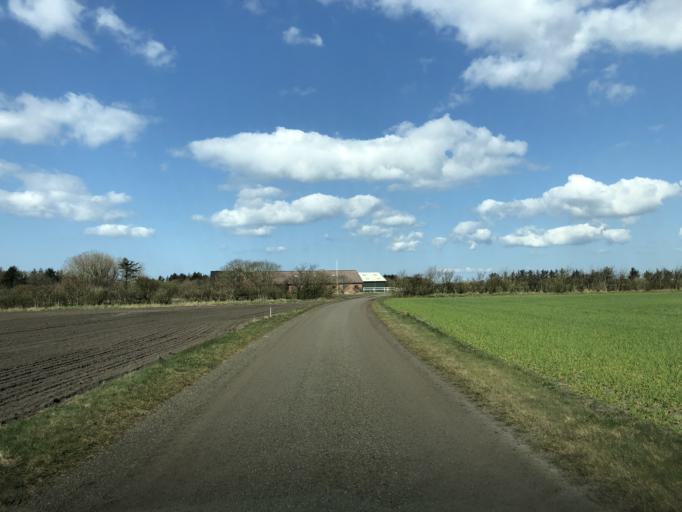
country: DK
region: Central Jutland
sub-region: Holstebro Kommune
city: Ulfborg
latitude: 56.3950
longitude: 8.1817
